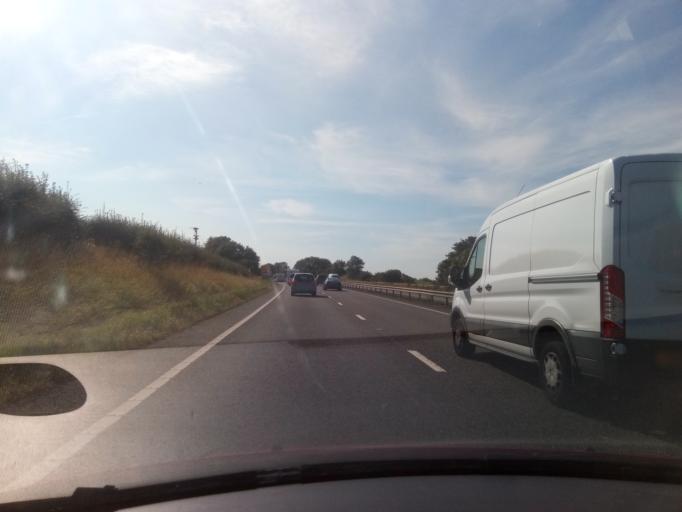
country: GB
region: England
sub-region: Hartlepool
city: Elwick
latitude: 54.6607
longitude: -1.3037
